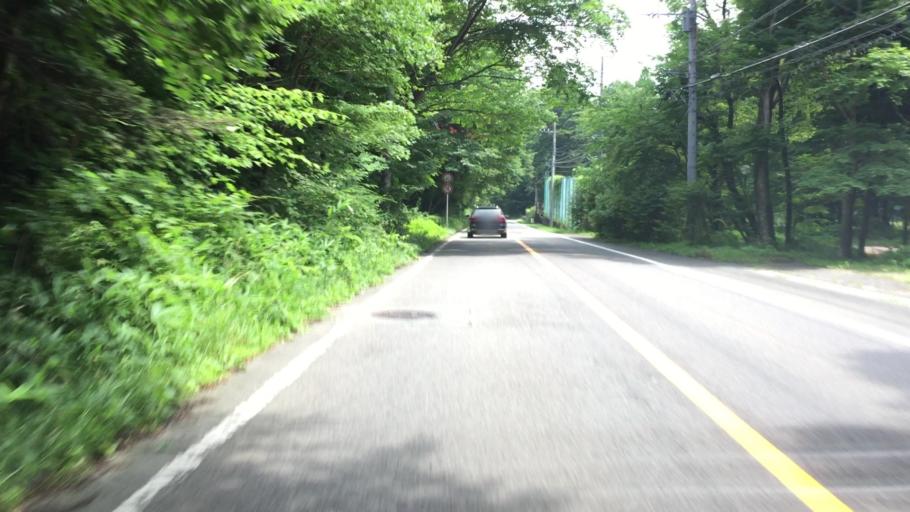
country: JP
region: Tochigi
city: Kuroiso
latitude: 37.0458
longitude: 139.9393
